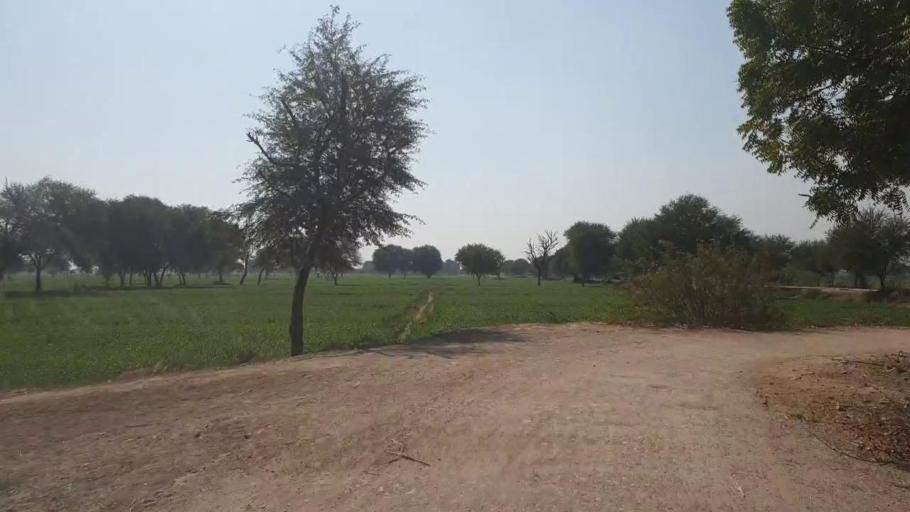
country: PK
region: Sindh
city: Tando Jam
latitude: 25.3017
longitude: 68.6348
